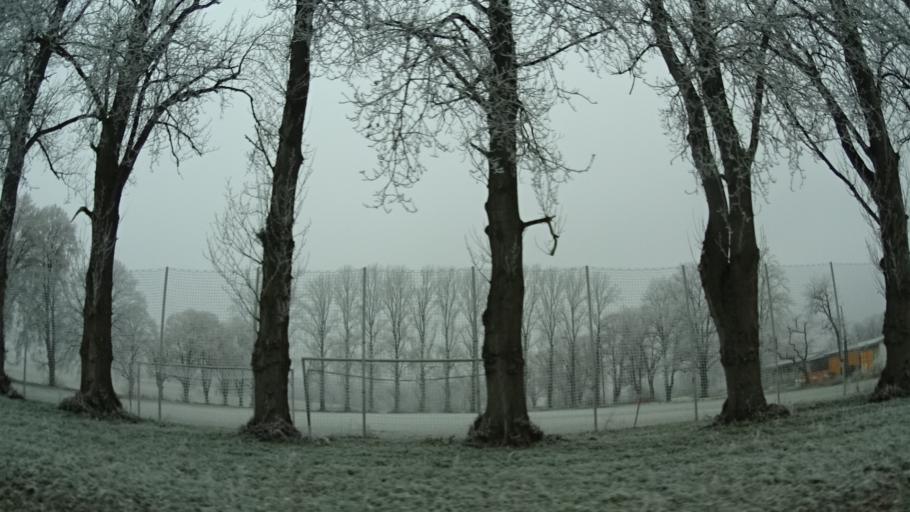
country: DE
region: Bavaria
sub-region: Regierungsbezirk Unterfranken
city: Hassfurt
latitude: 50.0272
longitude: 10.5061
